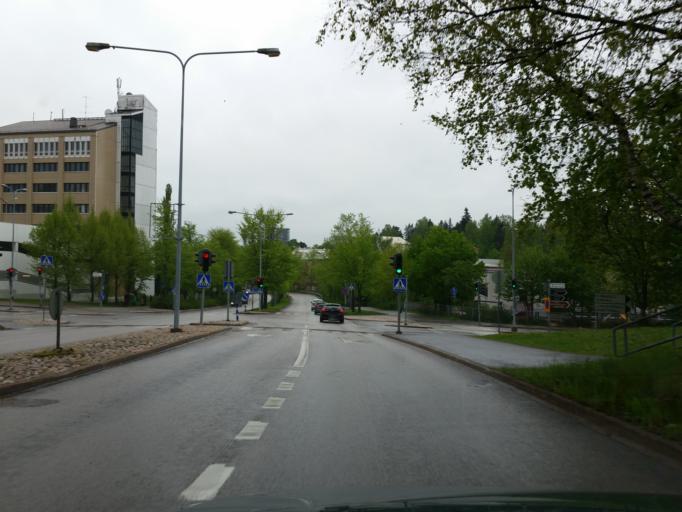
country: FI
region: Uusimaa
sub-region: Helsinki
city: Kilo
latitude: 60.2257
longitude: 24.8114
